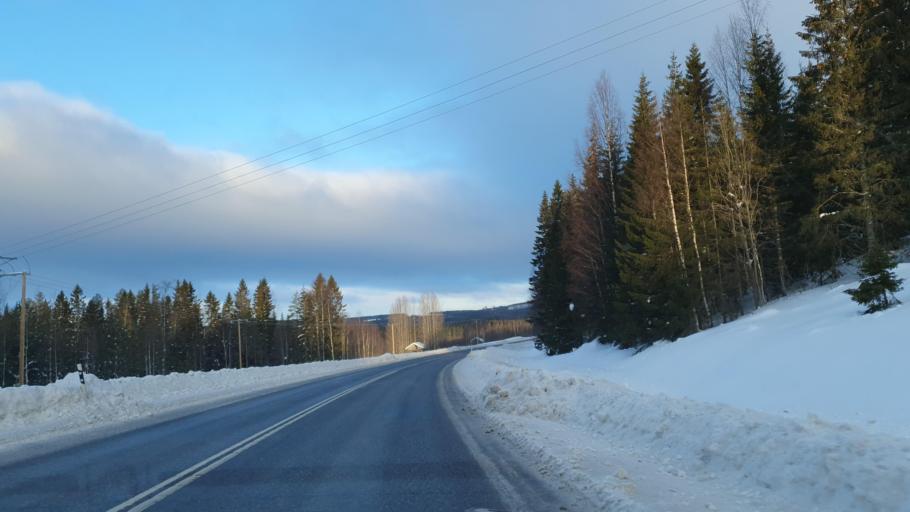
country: FI
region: Kainuu
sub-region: Kajaani
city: Kajaani
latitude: 64.4268
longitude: 27.5850
